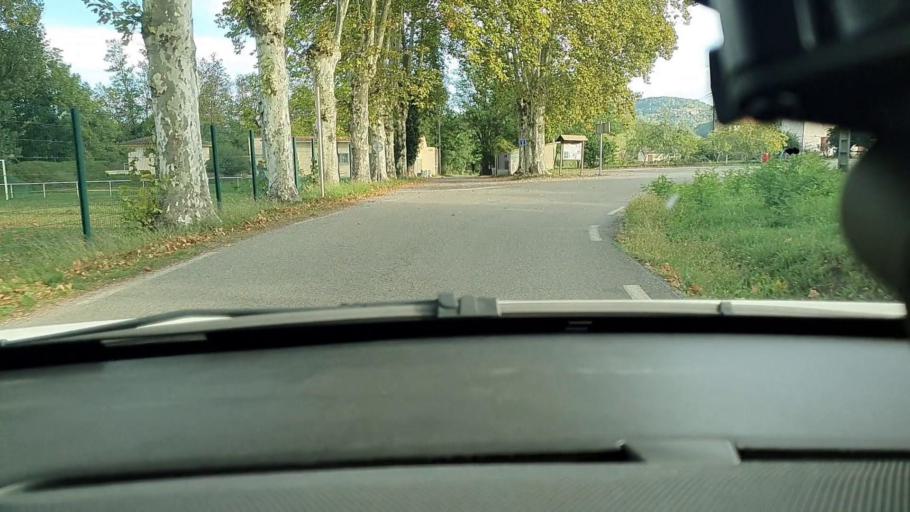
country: FR
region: Languedoc-Roussillon
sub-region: Departement du Gard
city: Besseges
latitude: 44.3160
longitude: 4.1309
